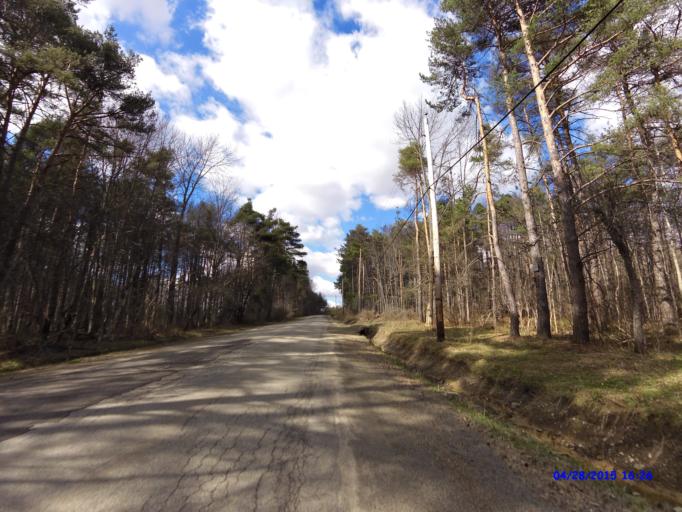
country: US
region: New York
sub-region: Cattaraugus County
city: Franklinville
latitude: 42.3817
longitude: -78.4419
